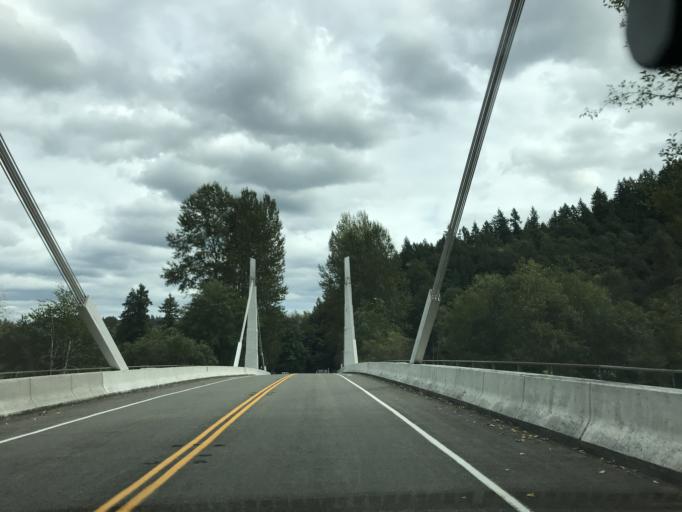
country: US
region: Washington
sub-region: King County
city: Black Diamond
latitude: 47.2788
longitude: -122.0394
